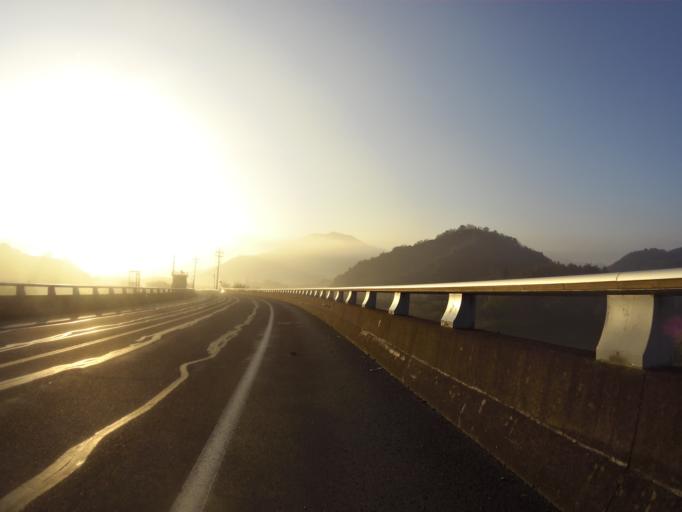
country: KR
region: Gyeongsangnam-do
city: Naeso
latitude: 35.3818
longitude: 128.5216
